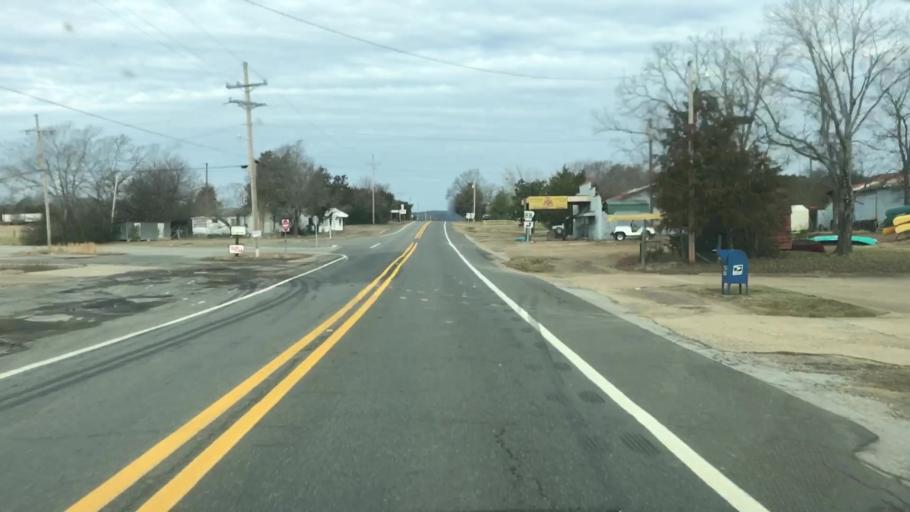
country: US
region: Arkansas
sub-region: Montgomery County
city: Mount Ida
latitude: 34.6293
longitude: -93.7335
